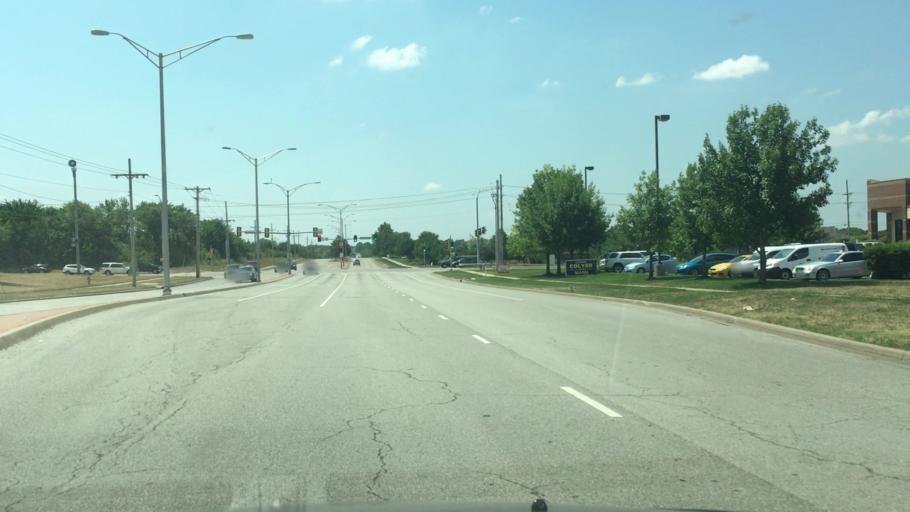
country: US
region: Kansas
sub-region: Johnson County
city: Lenexa
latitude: 38.8850
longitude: -94.7238
